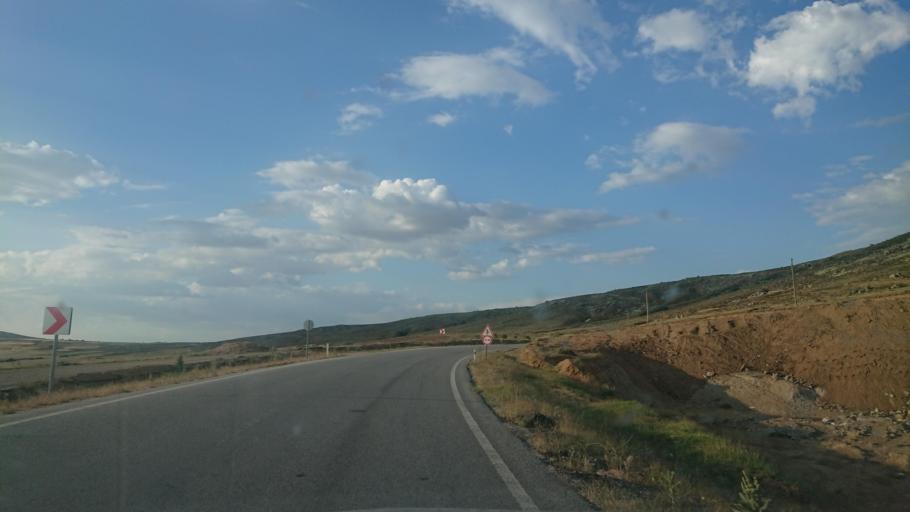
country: TR
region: Aksaray
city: Balci
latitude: 38.5972
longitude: 34.1015
